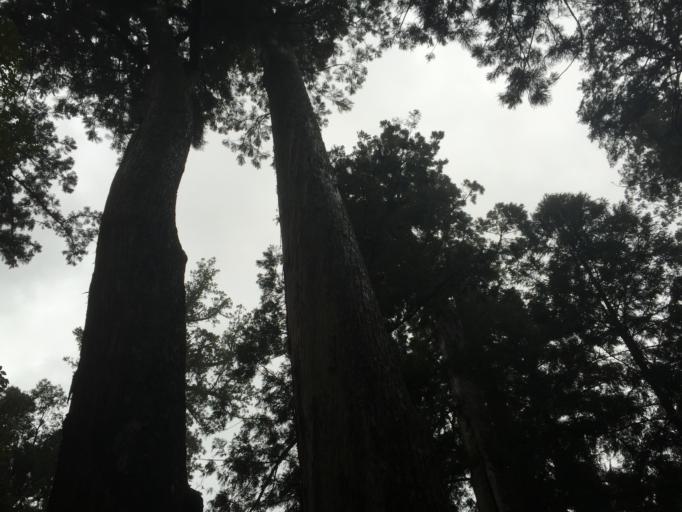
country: JP
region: Mie
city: Ise
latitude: 34.4541
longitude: 136.7250
